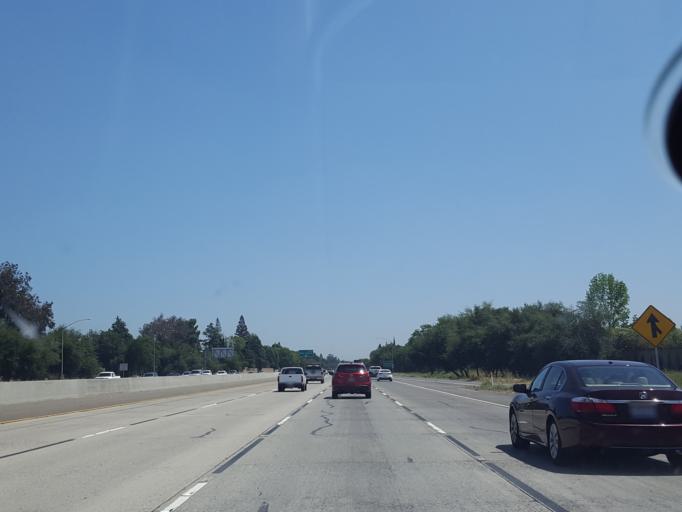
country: US
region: California
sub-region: Sacramento County
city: Rosemont
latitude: 38.5541
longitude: -121.4069
